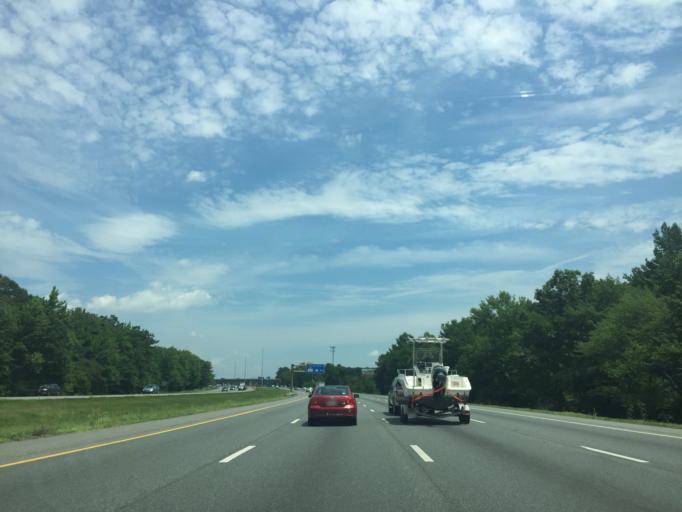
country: US
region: Delaware
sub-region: New Castle County
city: Brookside
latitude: 39.6548
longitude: -75.7034
